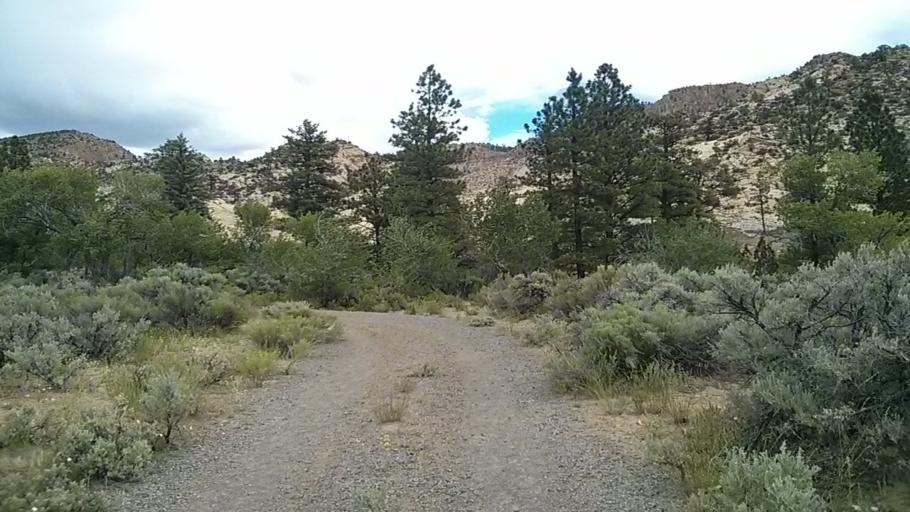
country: US
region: Utah
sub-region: Wayne County
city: Loa
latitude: 37.8622
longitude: -111.6364
